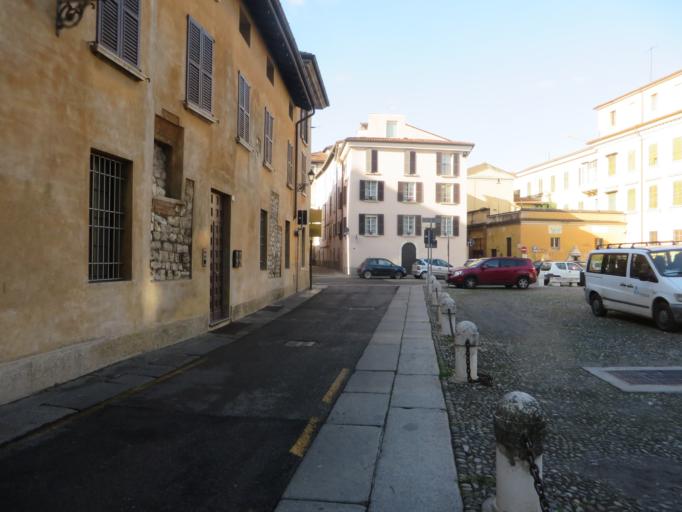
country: IT
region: Lombardy
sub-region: Provincia di Brescia
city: Brescia
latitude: 45.5345
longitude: 10.2256
